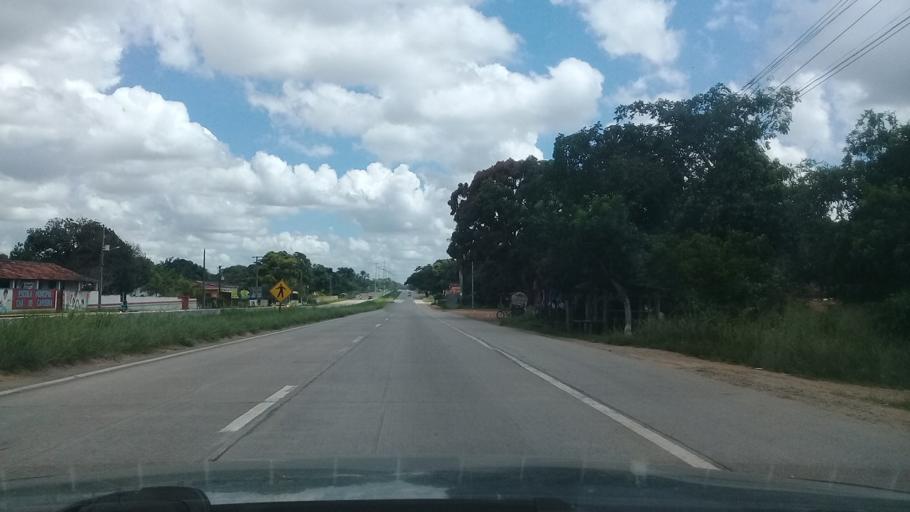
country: BR
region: Pernambuco
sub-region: Sao Lourenco Da Mata
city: Sao Lourenco da Mata
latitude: -7.9320
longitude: -35.1361
